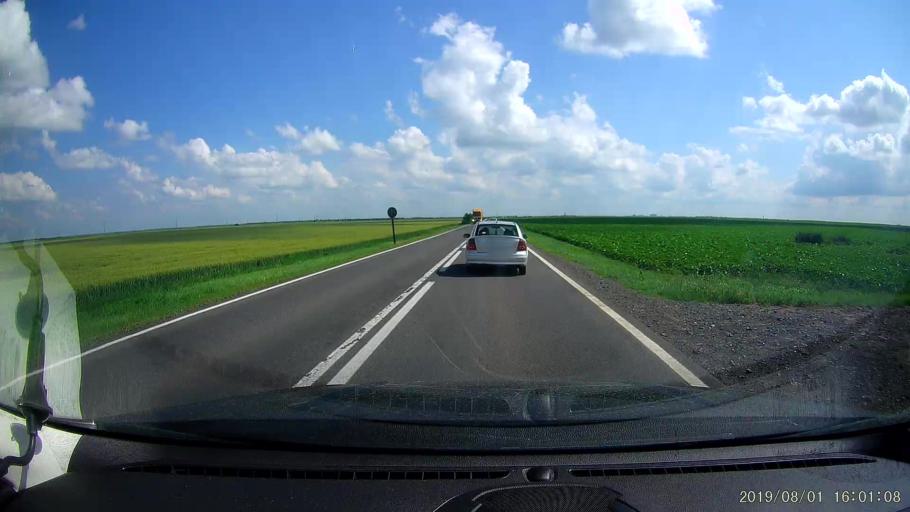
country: RO
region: Ialomita
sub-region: Comuna Ciulnita
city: Ciulnita
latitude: 44.5140
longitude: 27.3899
